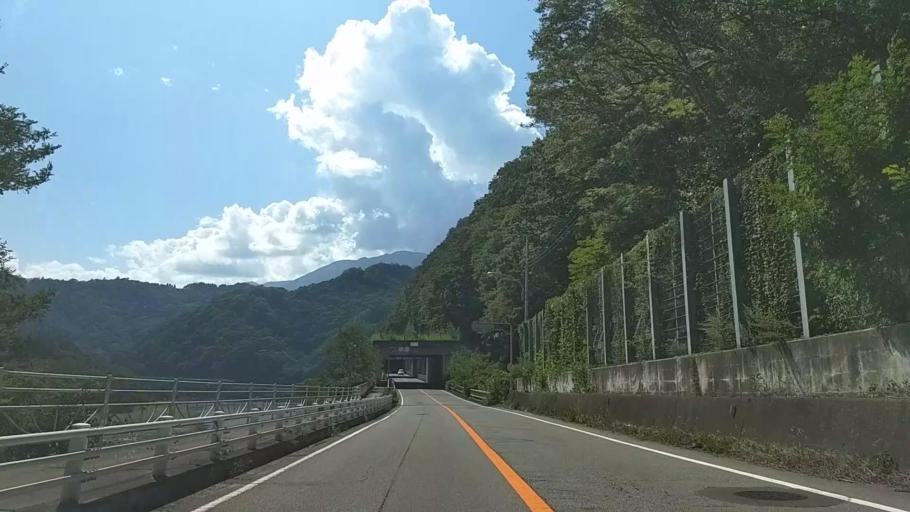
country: JP
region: Yamanashi
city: Ryuo
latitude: 35.5085
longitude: 138.4540
